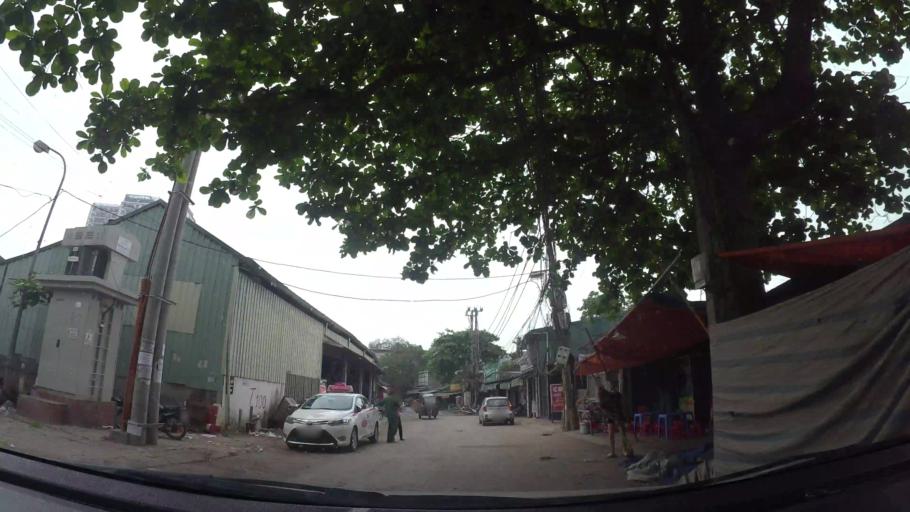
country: VN
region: Ha Noi
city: Tay Ho
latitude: 21.0690
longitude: 105.8285
